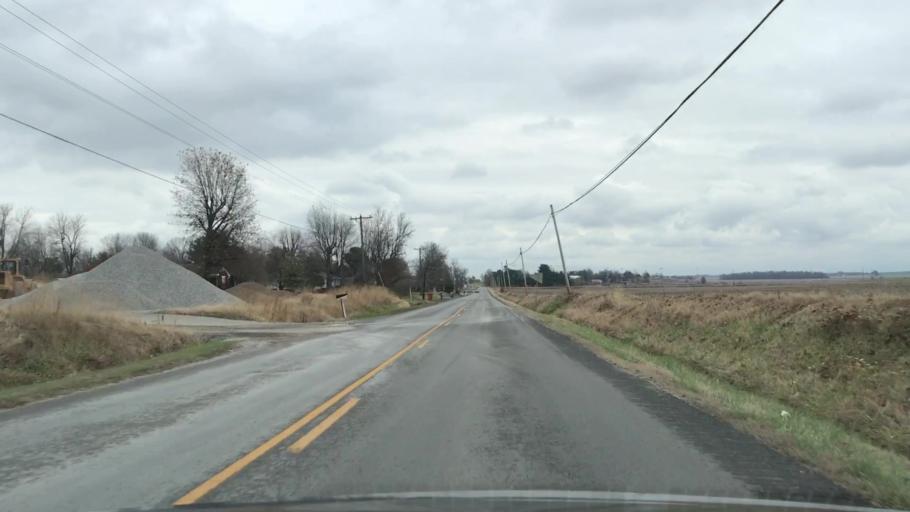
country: US
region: Kentucky
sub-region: McLean County
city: Calhoun
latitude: 37.5503
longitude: -87.2482
